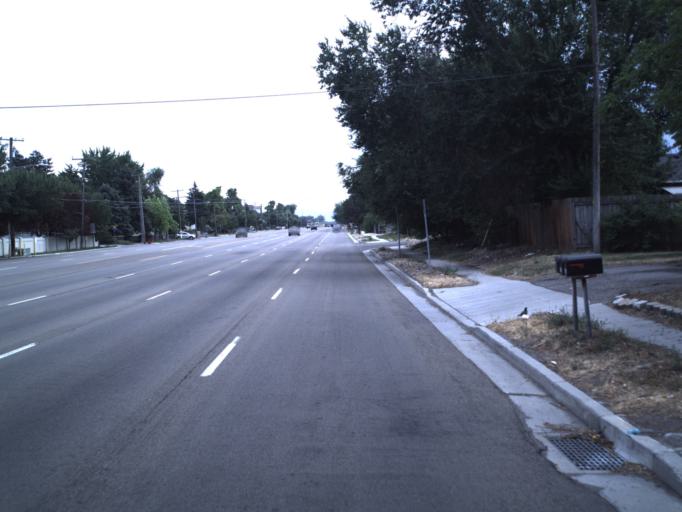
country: US
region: Utah
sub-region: Salt Lake County
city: Millcreek
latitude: 40.6982
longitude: -111.8715
